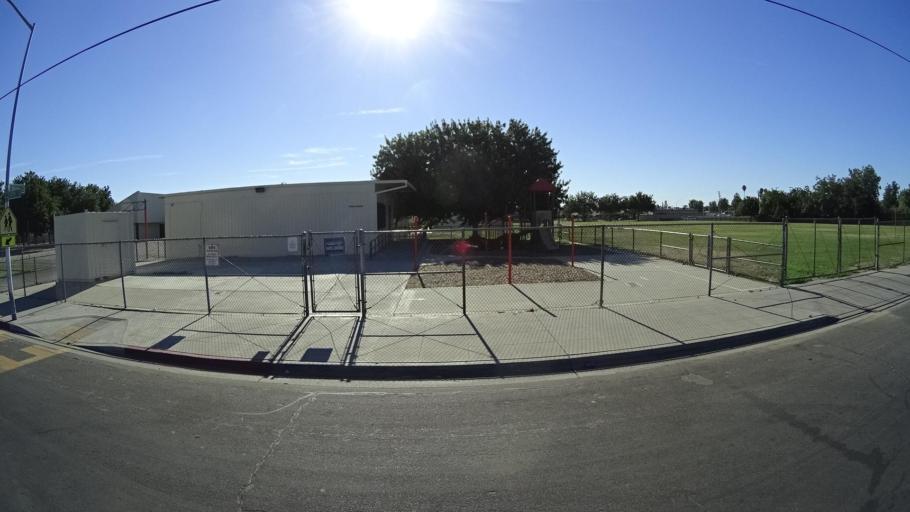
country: US
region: California
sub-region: Fresno County
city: Fresno
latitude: 36.7520
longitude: -119.7658
